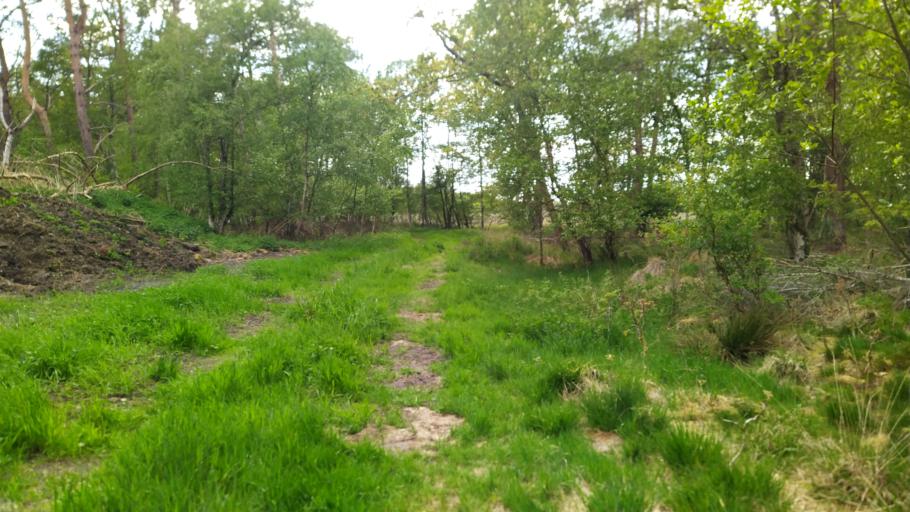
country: DE
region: Lower Saxony
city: Brest
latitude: 53.4317
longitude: 9.3918
